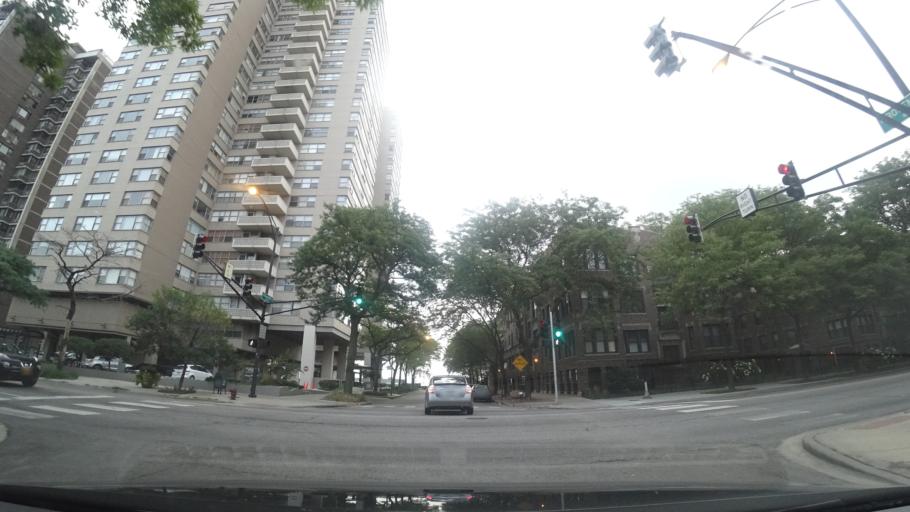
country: US
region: Illinois
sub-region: Cook County
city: Evanston
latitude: 41.9964
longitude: -87.6557
